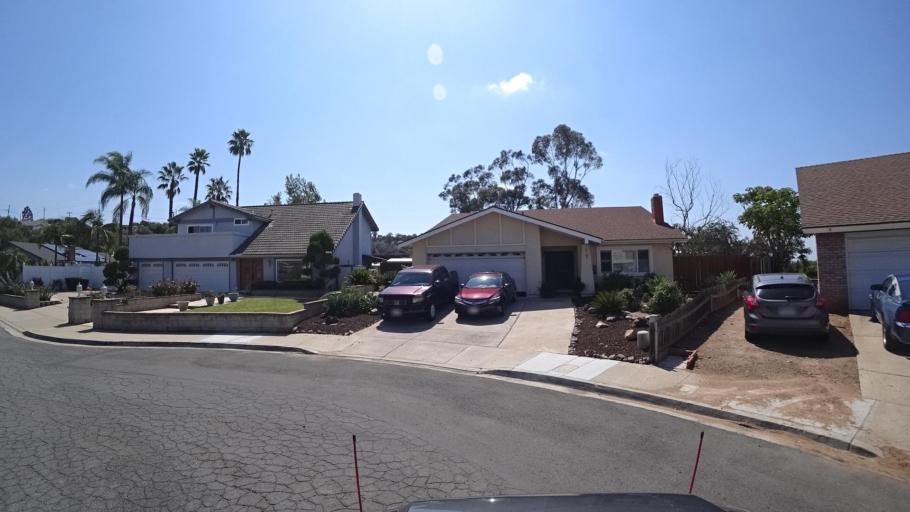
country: US
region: California
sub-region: San Diego County
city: Spring Valley
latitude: 32.7429
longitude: -116.9866
